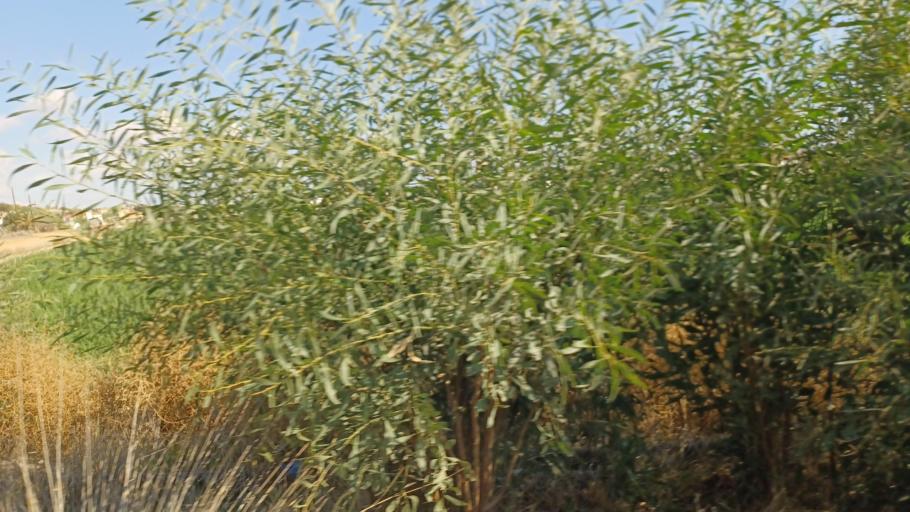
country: CY
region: Larnaka
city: Voroklini
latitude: 34.9950
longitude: 33.6693
